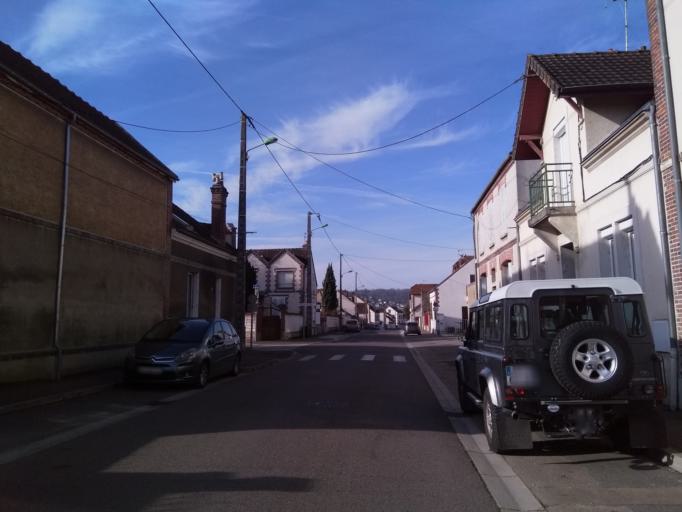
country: FR
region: Bourgogne
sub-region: Departement de l'Yonne
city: Sens
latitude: 48.1910
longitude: 3.2791
